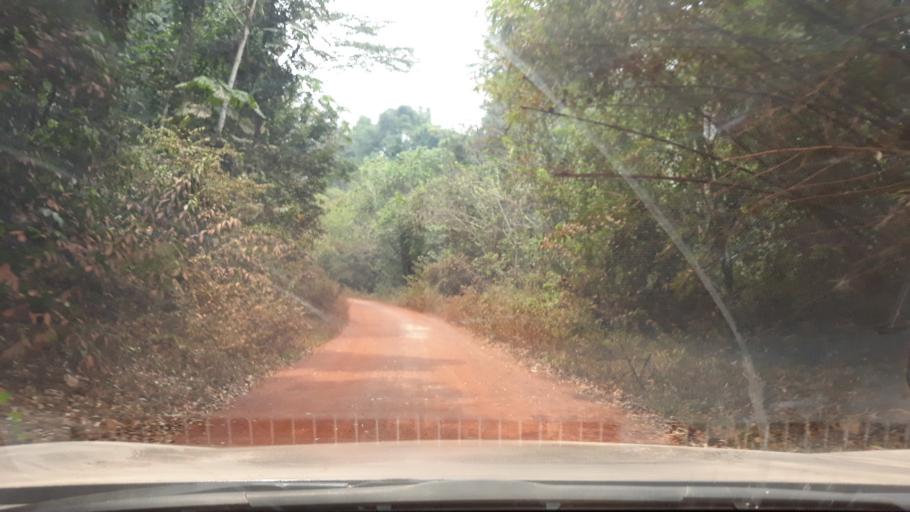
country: CD
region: Eastern Province
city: Buta
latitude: 2.3146
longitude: 25.0033
